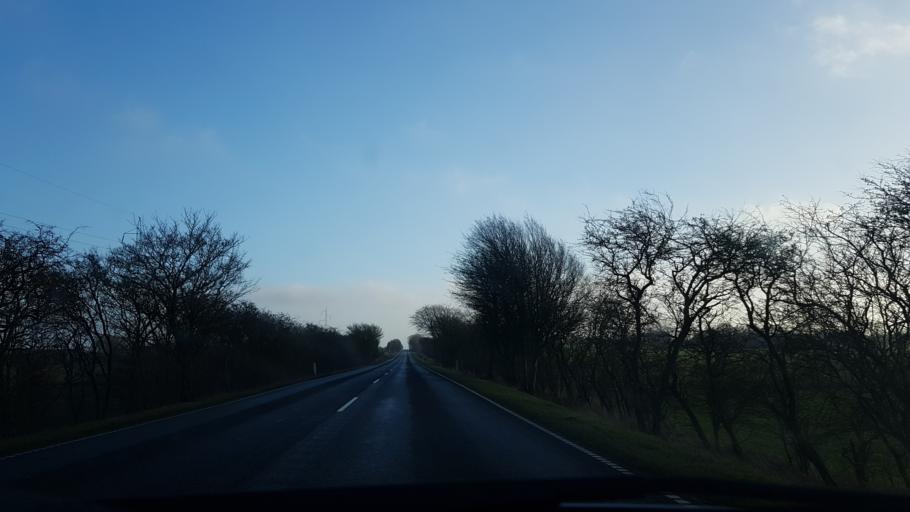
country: DK
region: South Denmark
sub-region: Haderslev Kommune
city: Vojens
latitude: 55.1918
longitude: 9.2110
